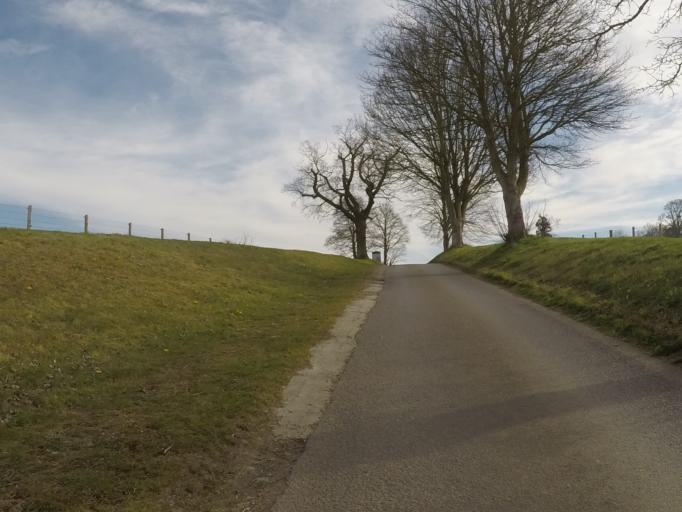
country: GB
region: England
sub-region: Oxfordshire
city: Charlbury
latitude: 51.8518
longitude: -1.4728
